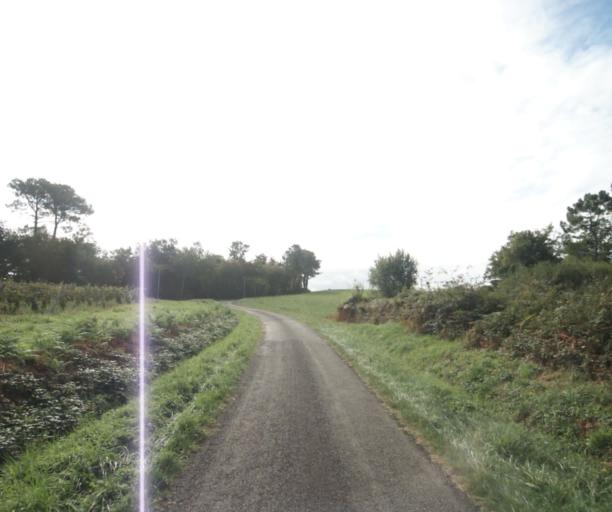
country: FR
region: Midi-Pyrenees
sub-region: Departement du Gers
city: Cazaubon
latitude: 43.8499
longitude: -0.0785
